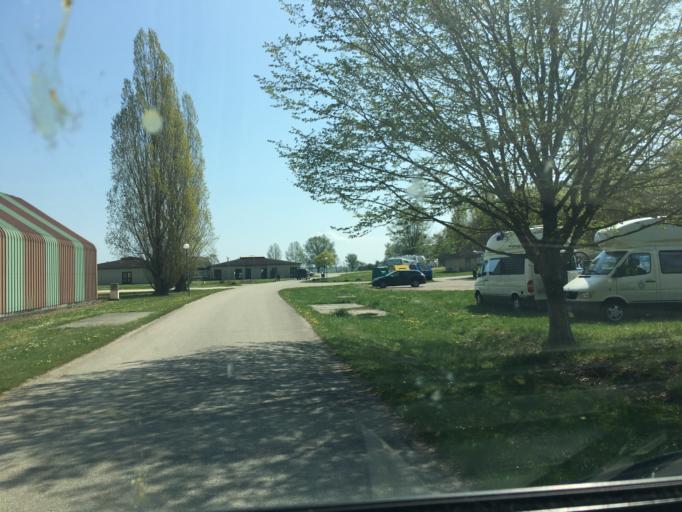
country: FR
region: Lorraine
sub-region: Departement de la Meuse
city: Vigneulles-les-Hattonchatel
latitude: 48.9366
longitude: 5.7140
